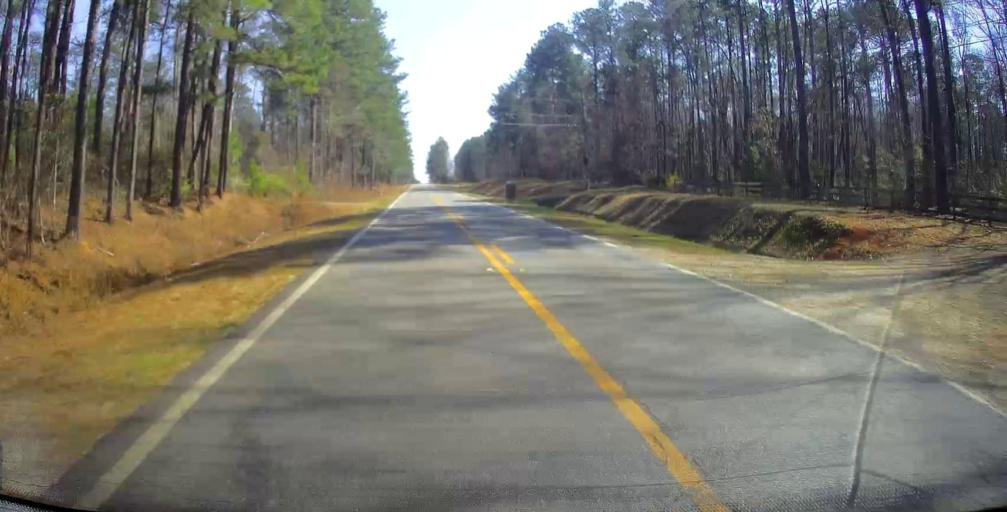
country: US
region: Georgia
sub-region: Jones County
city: Gray
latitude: 32.9478
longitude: -83.5422
